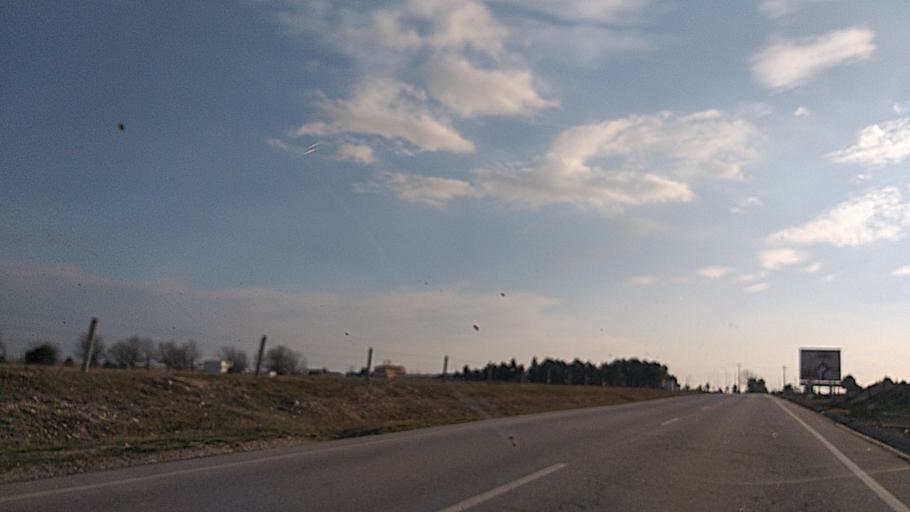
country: ES
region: Castille and Leon
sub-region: Provincia de Salamanca
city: Fuentes de Onoro
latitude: 40.5990
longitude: -6.9904
